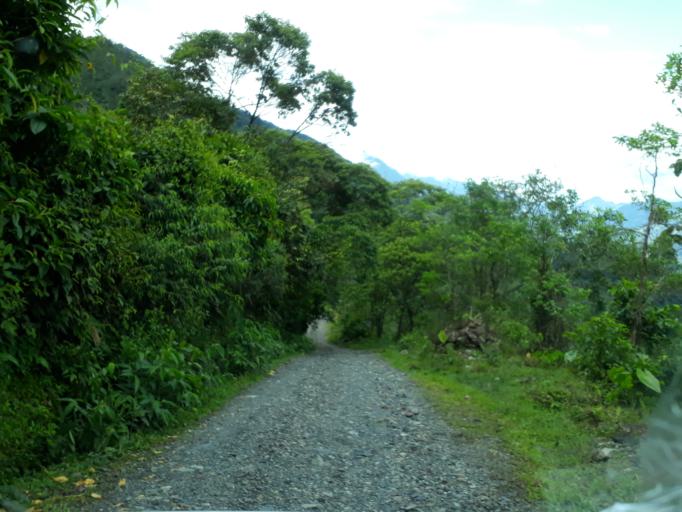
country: CO
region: Cundinamarca
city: Gachala
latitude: 4.7170
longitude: -73.3619
